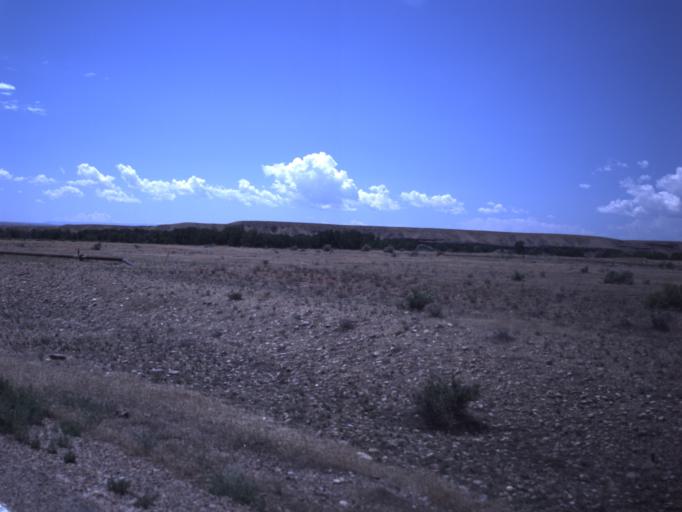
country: US
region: Utah
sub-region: Duchesne County
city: Roosevelt
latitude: 40.0963
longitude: -109.6798
